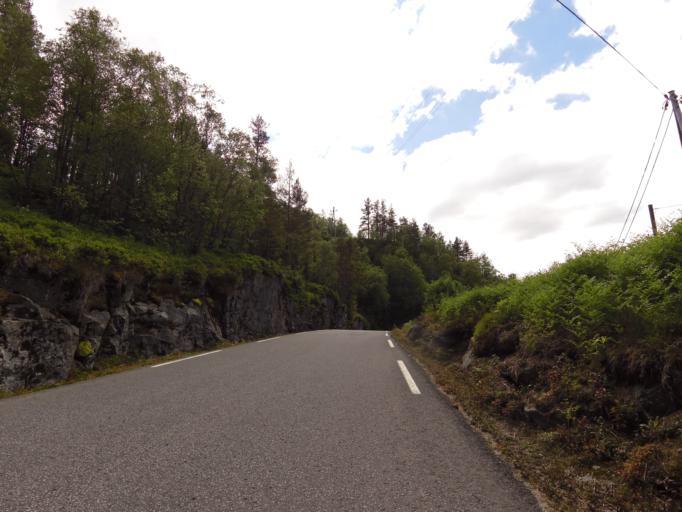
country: NO
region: Vest-Agder
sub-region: Kvinesdal
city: Liknes
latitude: 58.2837
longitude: 6.9288
